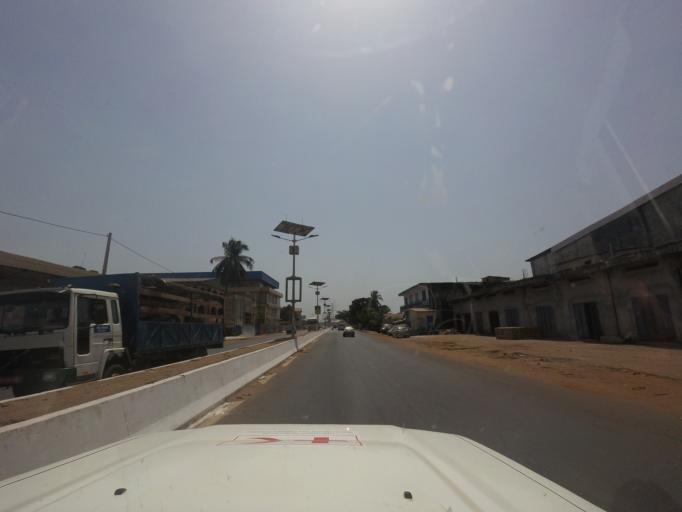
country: GN
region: Conakry
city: Conakry
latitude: 9.5549
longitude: -13.6536
